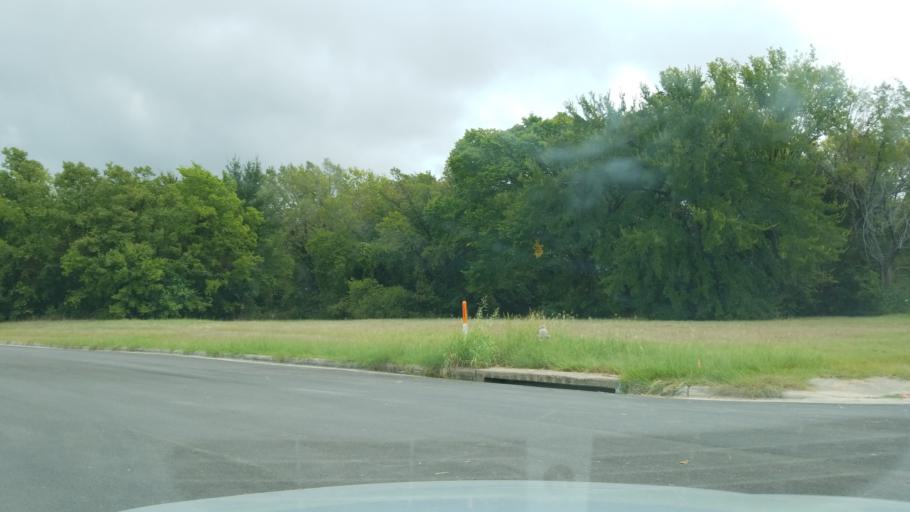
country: US
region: Texas
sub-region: Tarrant County
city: Bedford
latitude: 32.8348
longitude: -97.1175
